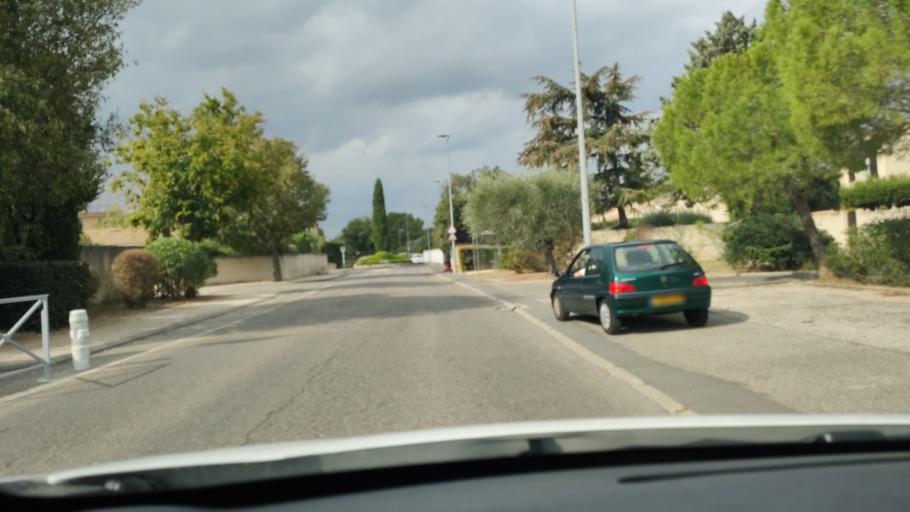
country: FR
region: Languedoc-Roussillon
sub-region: Departement du Gard
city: Les Angles
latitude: 43.9595
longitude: 4.7668
